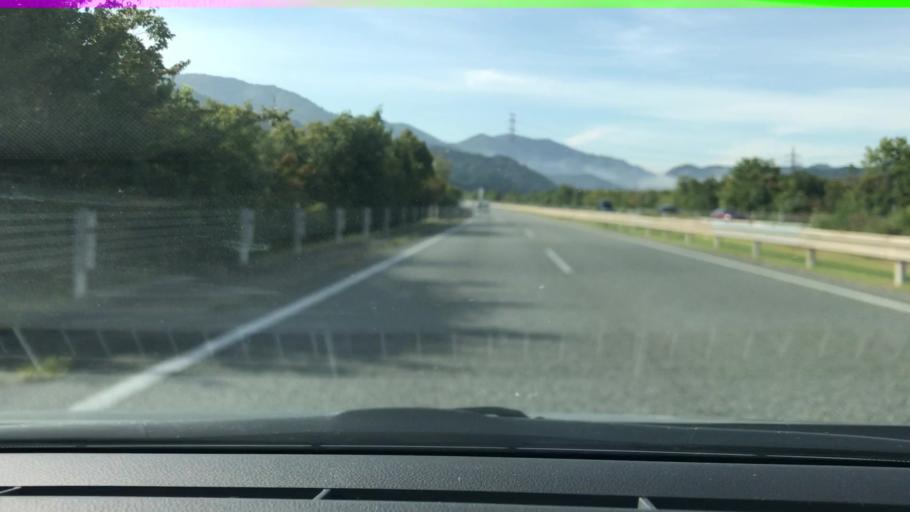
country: JP
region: Hyogo
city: Sasayama
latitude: 35.0508
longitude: 135.1832
